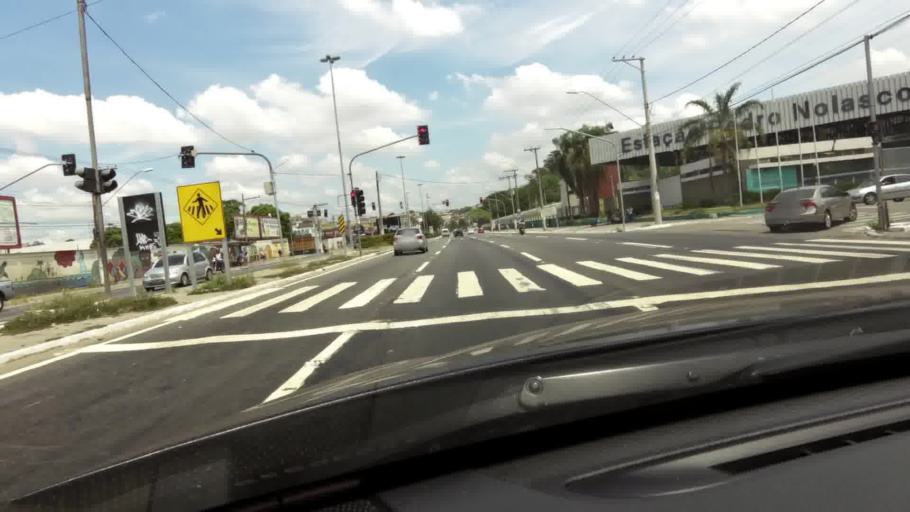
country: BR
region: Espirito Santo
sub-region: Vitoria
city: Vitoria
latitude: -20.3326
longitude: -40.3609
